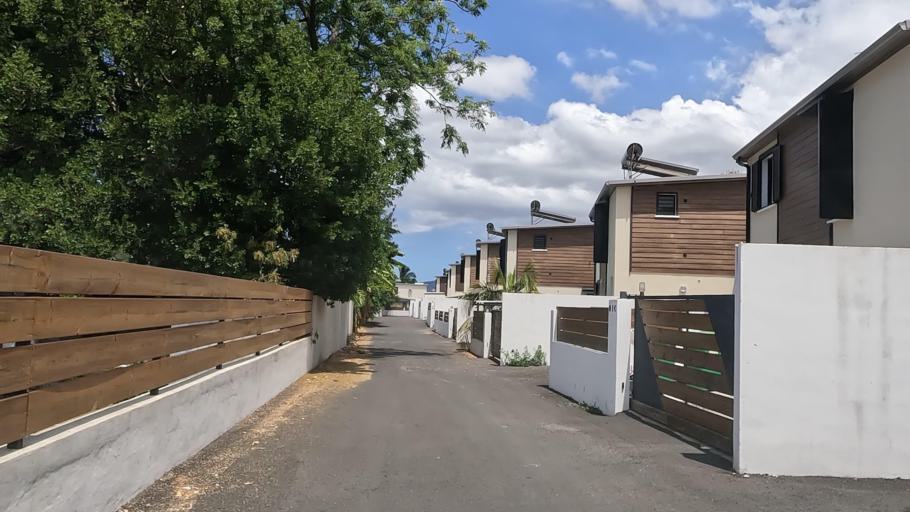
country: RE
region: Reunion
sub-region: Reunion
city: Saint-Louis
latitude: -21.2799
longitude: 55.4438
